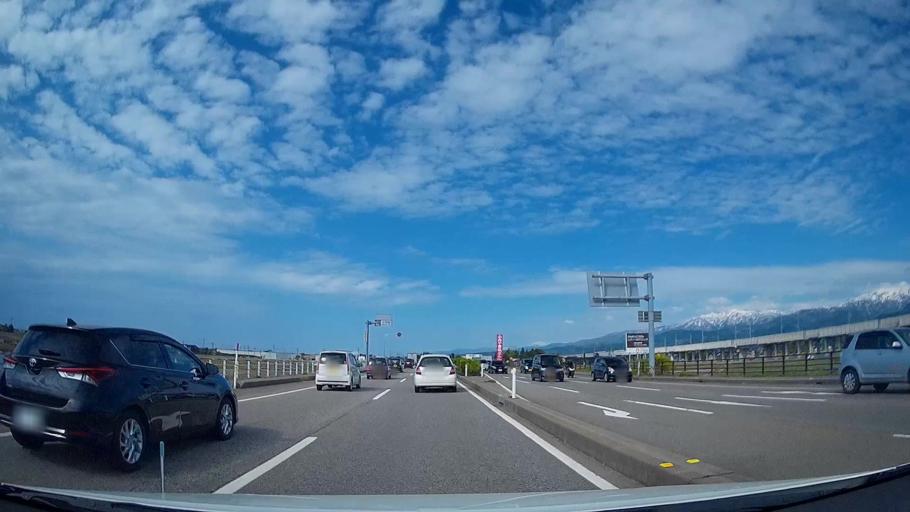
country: JP
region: Toyama
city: Namerikawa
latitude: 36.7339
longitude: 137.3351
